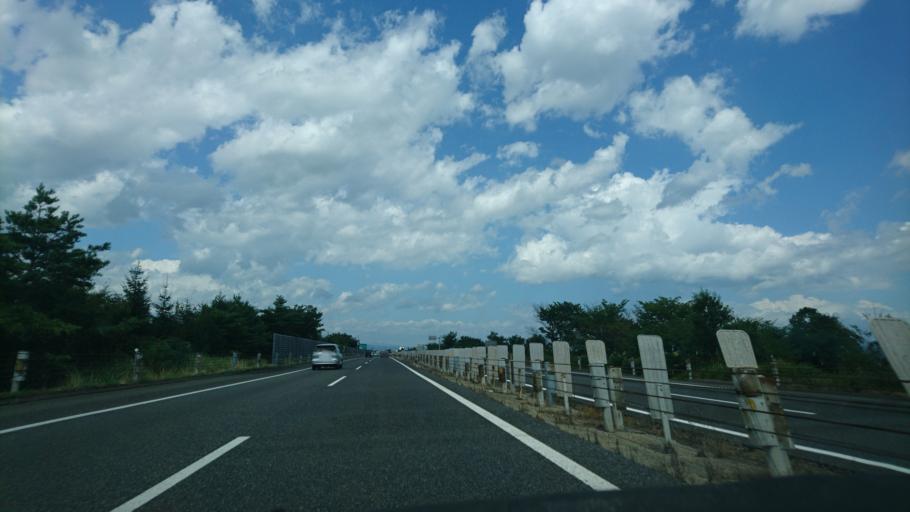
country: JP
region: Iwate
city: Morioka-shi
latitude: 39.6383
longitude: 141.1262
